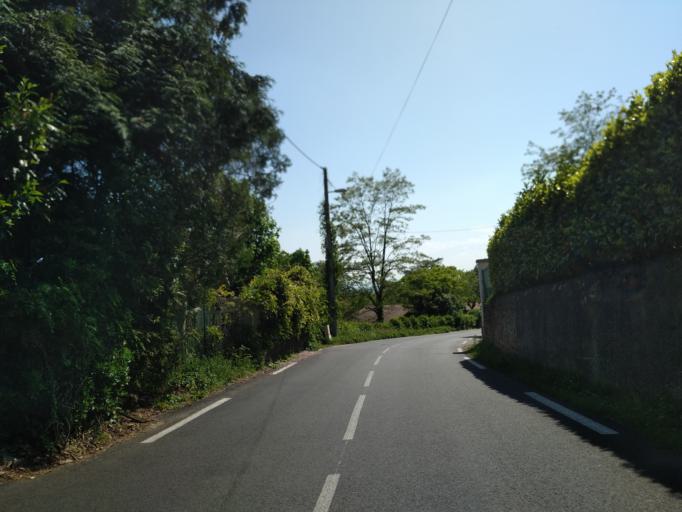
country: FR
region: Rhone-Alpes
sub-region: Departement du Rhone
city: Fontaines-sur-Saone
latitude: 45.8200
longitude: 4.8233
